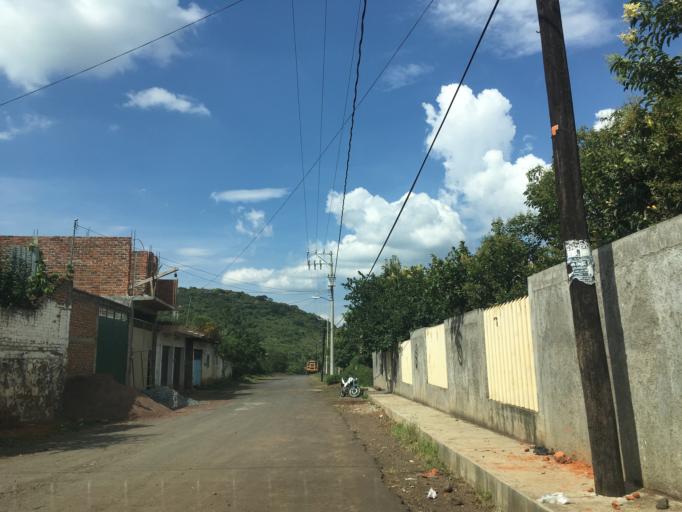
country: MX
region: Mexico
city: El Guayabito
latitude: 19.8998
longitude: -102.4971
